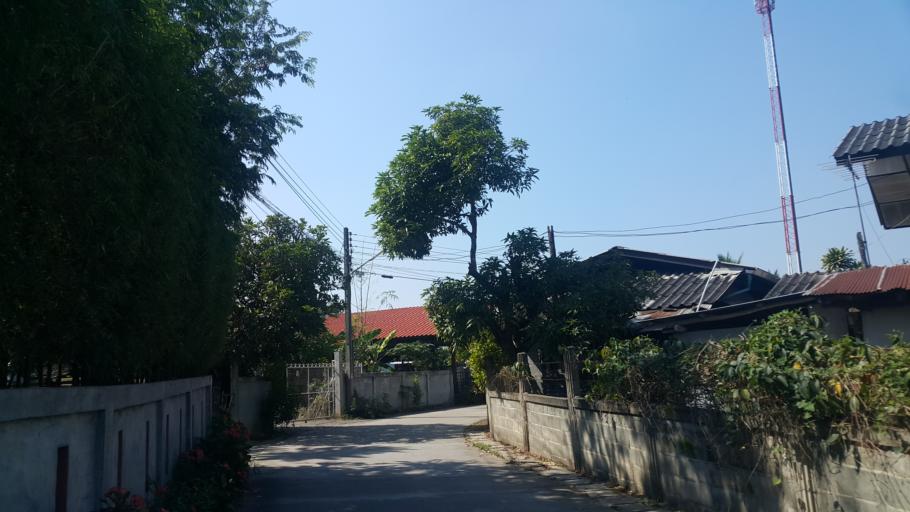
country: TH
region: Chiang Mai
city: San Kamphaeng
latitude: 18.6931
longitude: 99.1603
